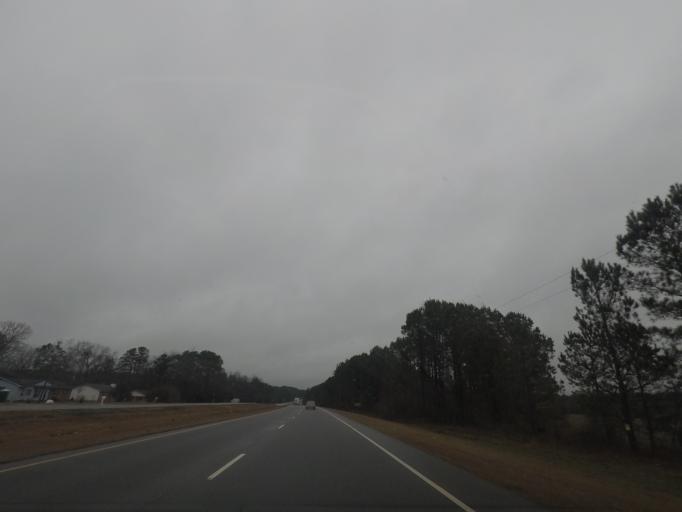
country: US
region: North Carolina
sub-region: Lee County
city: Broadway
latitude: 35.3209
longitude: -79.0911
